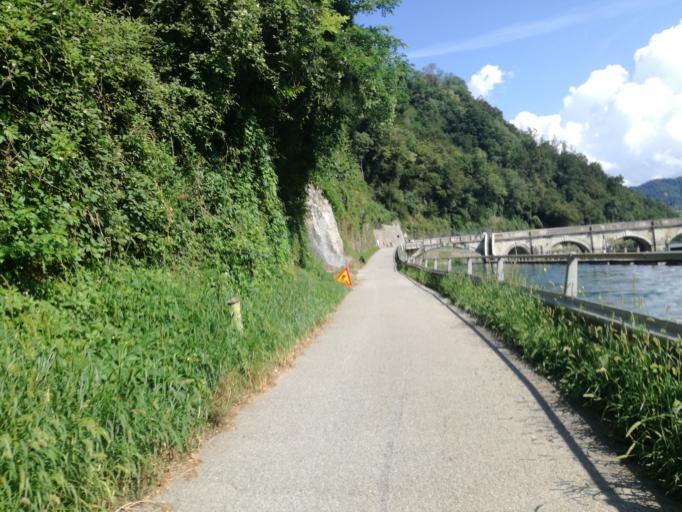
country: IT
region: Lombardy
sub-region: Provincia di Lecco
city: Paderno d'Adda
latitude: 45.6878
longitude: 9.4511
